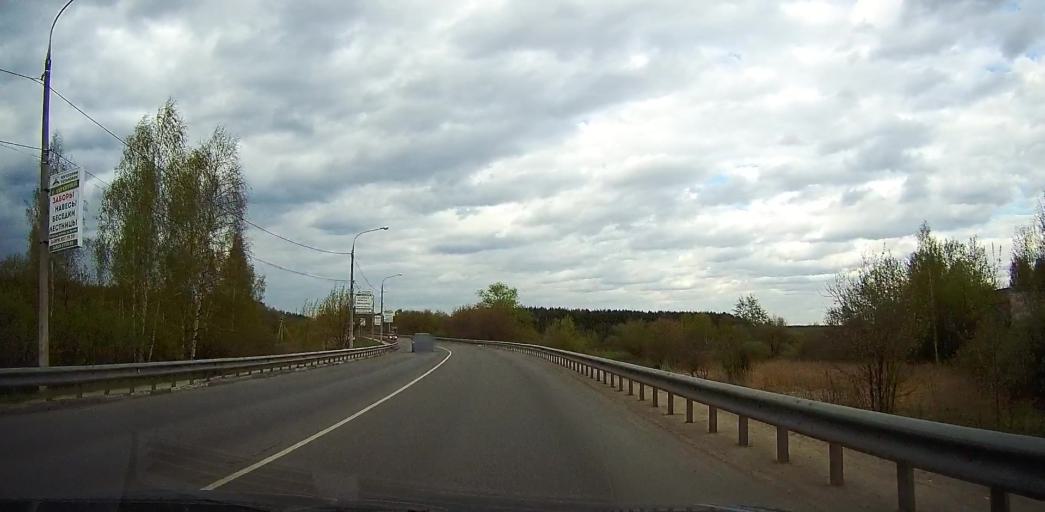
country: RU
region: Moskovskaya
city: Pavlovskiy Posad
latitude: 55.7952
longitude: 38.6528
